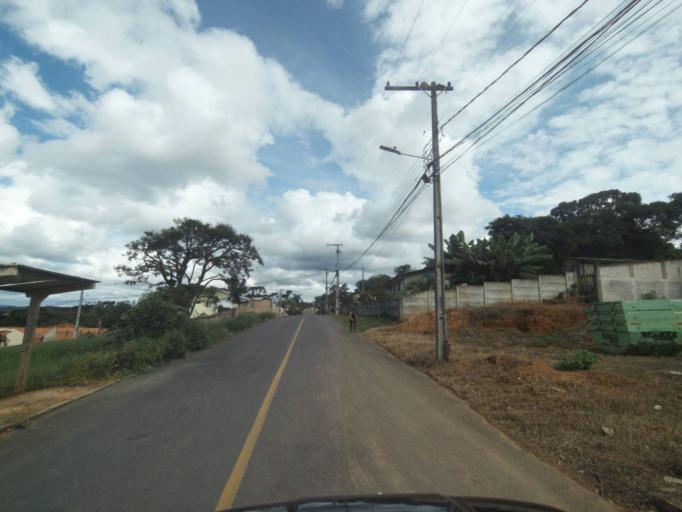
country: BR
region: Parana
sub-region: Telemaco Borba
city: Telemaco Borba
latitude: -24.3144
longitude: -50.6333
